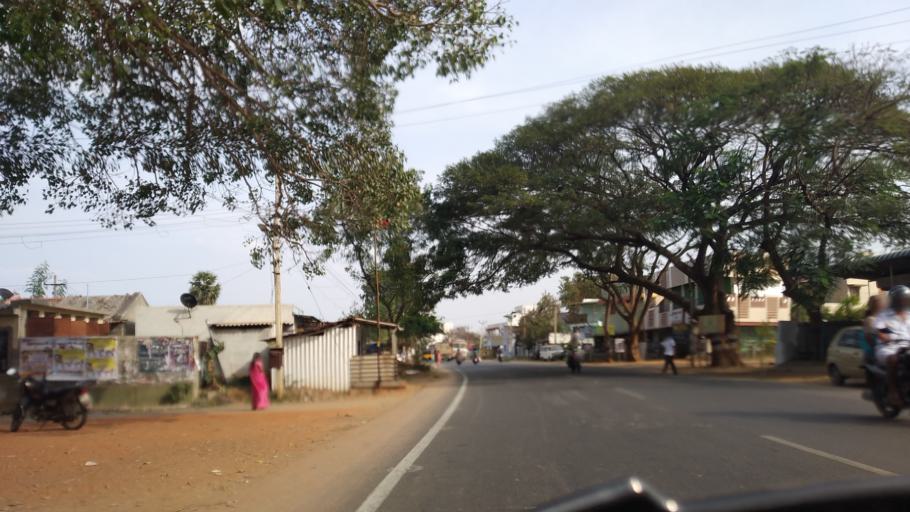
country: IN
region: Tamil Nadu
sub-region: Coimbatore
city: Perur
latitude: 10.9698
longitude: 76.8971
